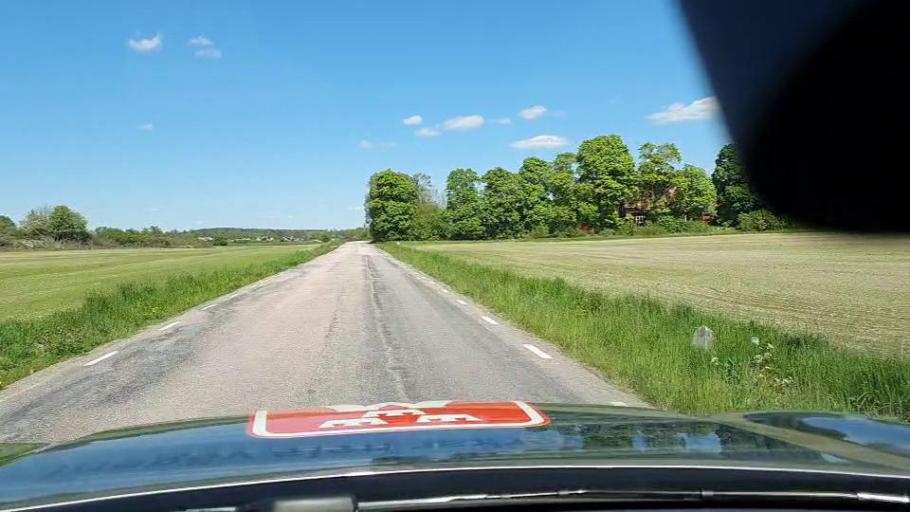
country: SE
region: Vaestmanland
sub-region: Hallstahammars Kommun
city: Kolback
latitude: 59.5350
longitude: 16.2978
